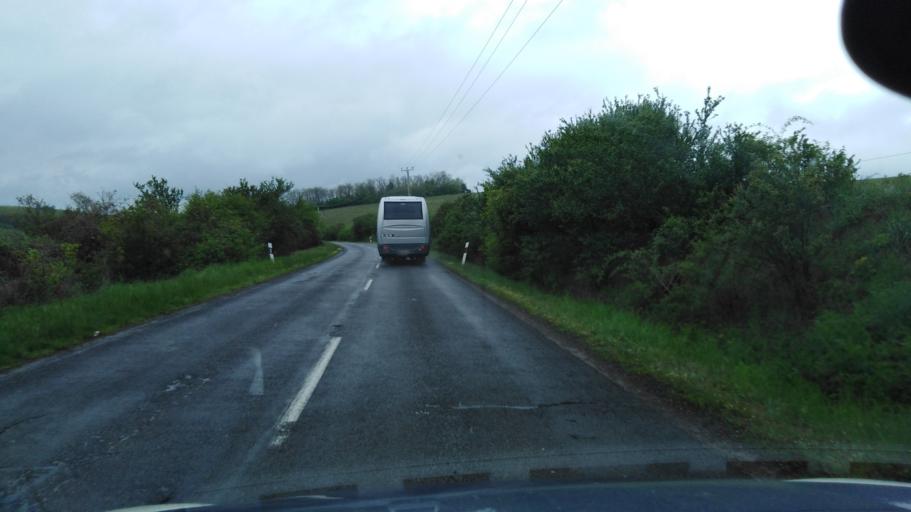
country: HU
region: Nograd
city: Rimoc
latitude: 48.0090
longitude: 19.6066
